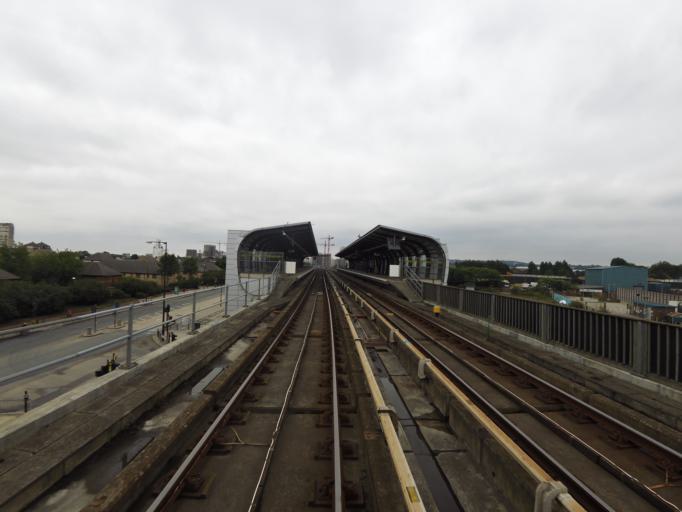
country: GB
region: England
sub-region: Greater London
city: Poplar
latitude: 51.5032
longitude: 0.0214
